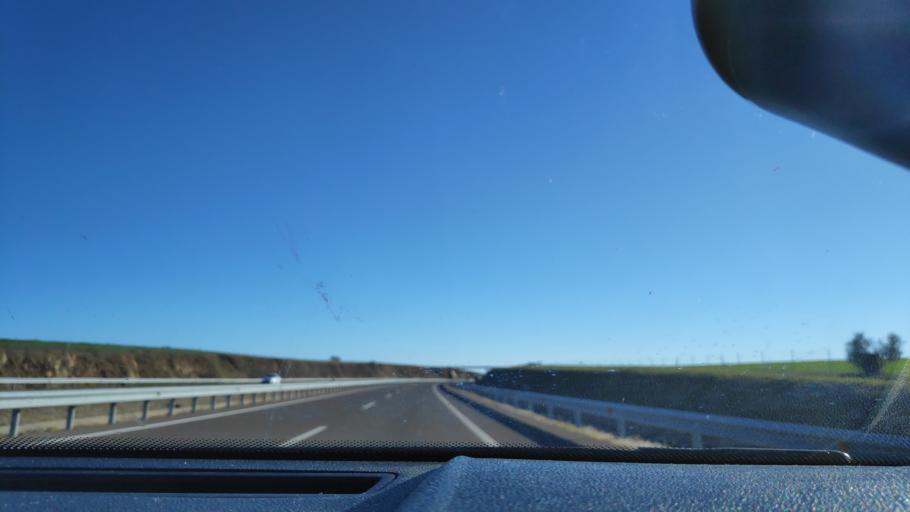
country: ES
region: Extremadura
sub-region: Provincia de Badajoz
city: Fuente de Cantos
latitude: 38.1940
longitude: -6.2818
